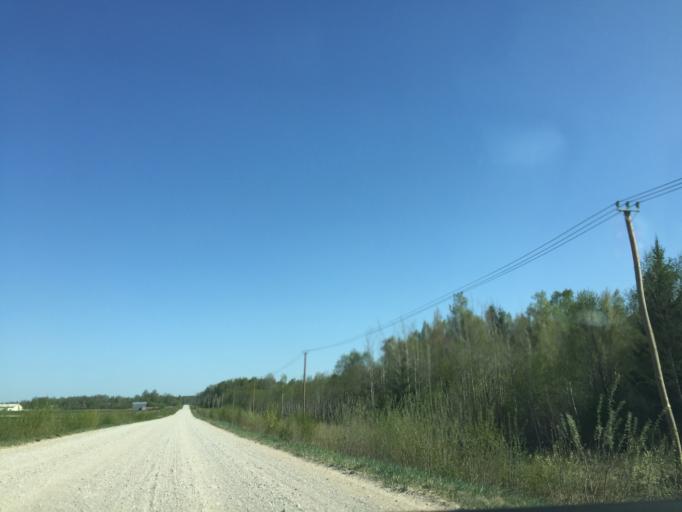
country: LV
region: Ogre
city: Jumprava
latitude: 56.8466
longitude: 25.0827
